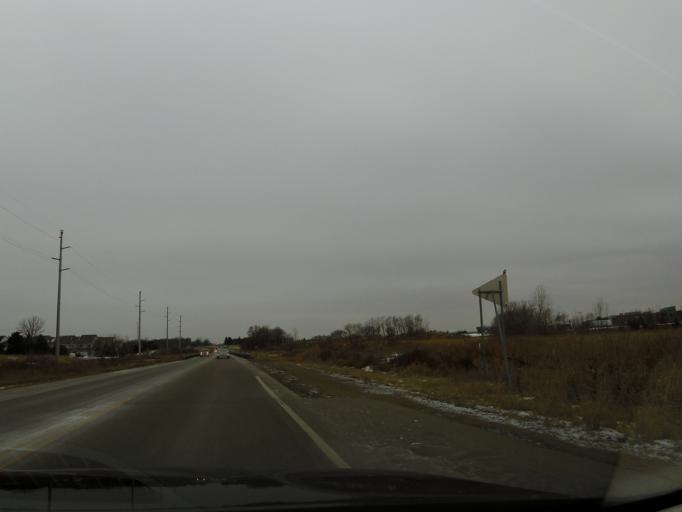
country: US
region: Minnesota
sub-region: Carver County
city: Waconia
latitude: 44.8335
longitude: -93.8133
